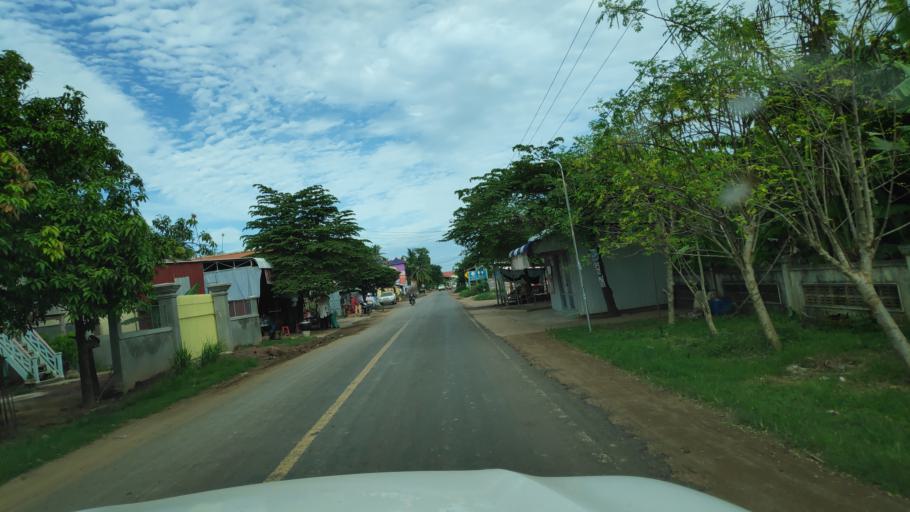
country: KH
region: Kampong Cham
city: Kampong Cham
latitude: 11.9465
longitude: 105.2491
